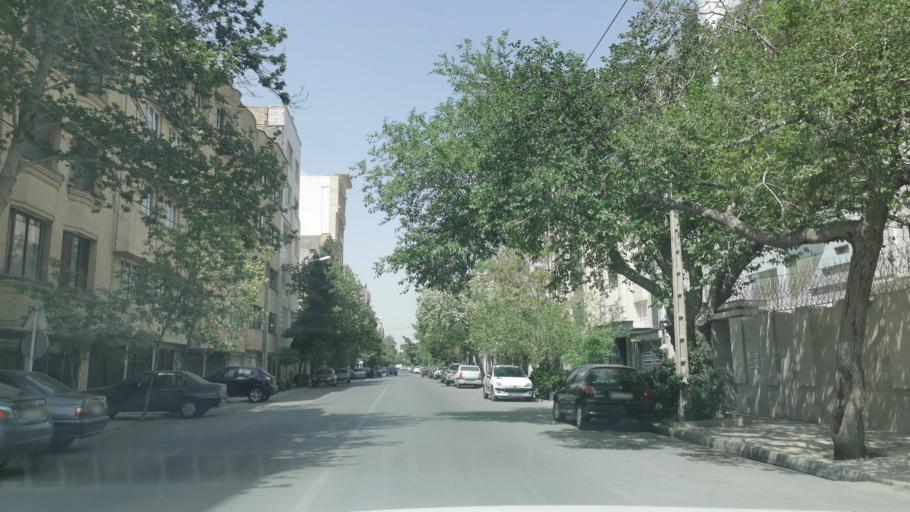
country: IR
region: Razavi Khorasan
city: Mashhad
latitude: 36.3098
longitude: 59.5625
